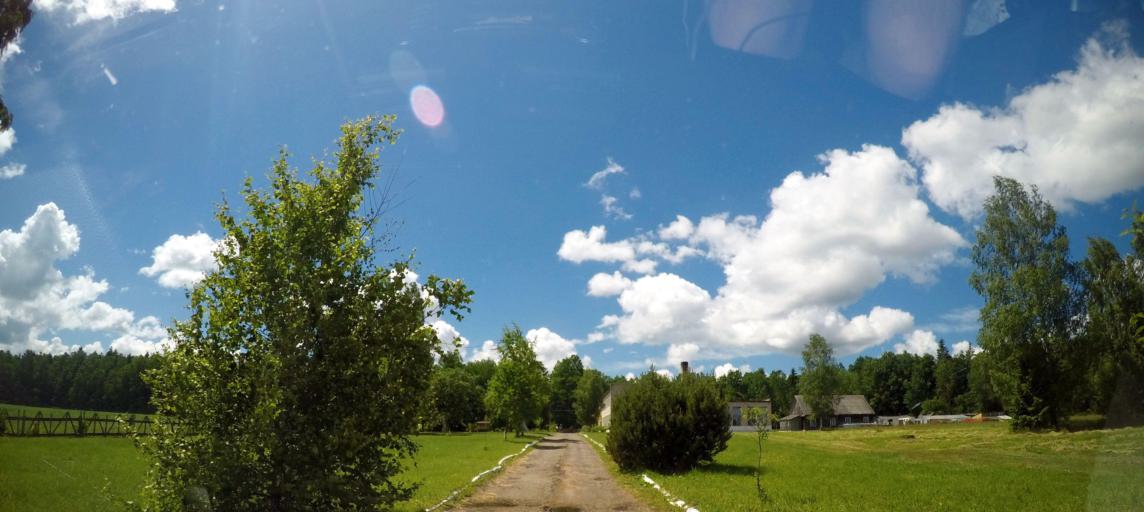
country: BY
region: Grodnenskaya
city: Hal'shany
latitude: 54.1674
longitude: 26.0811
